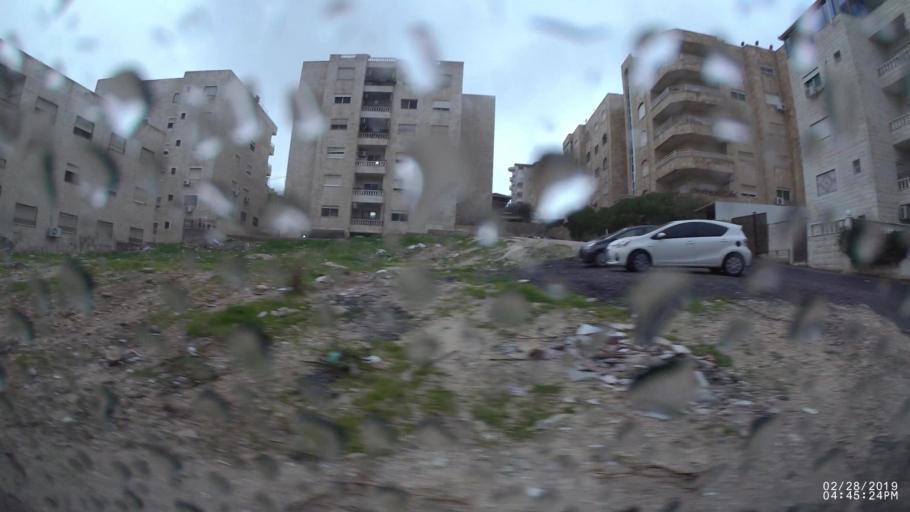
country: JO
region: Amman
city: Amman
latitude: 32.0049
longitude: 35.9313
